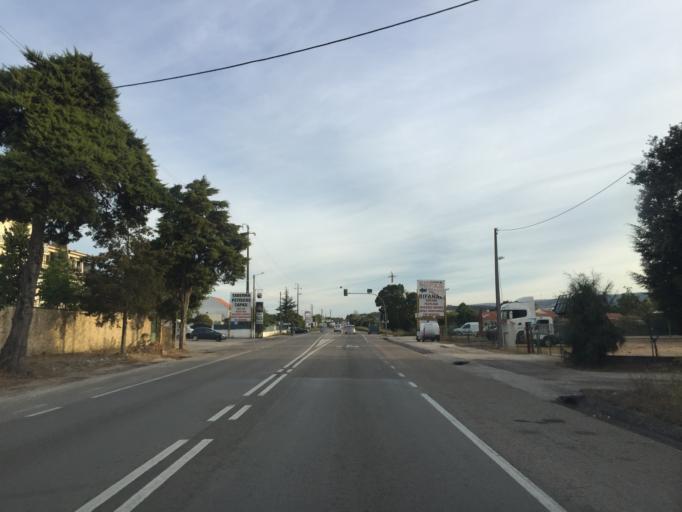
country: PT
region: Leiria
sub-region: Alcobaca
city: Benedita
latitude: 39.4264
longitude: -8.9599
